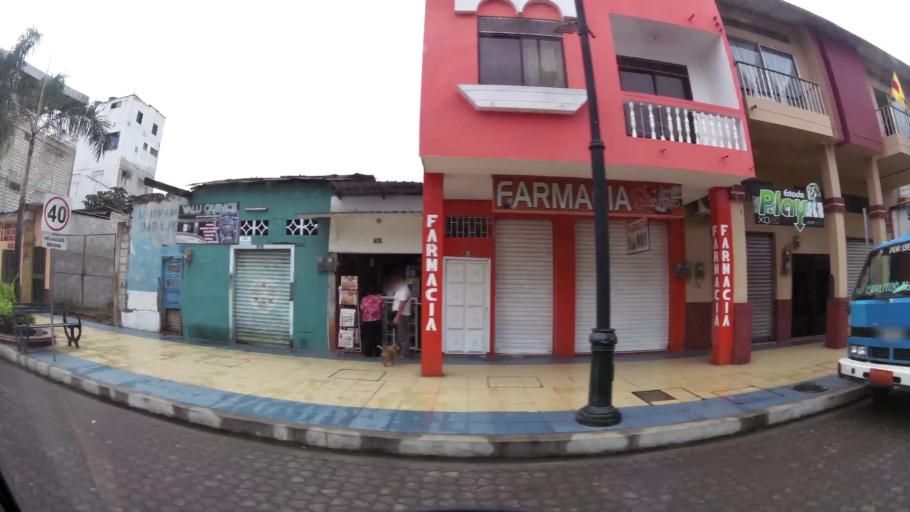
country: EC
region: El Oro
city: Pasaje
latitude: -3.3285
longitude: -79.8113
